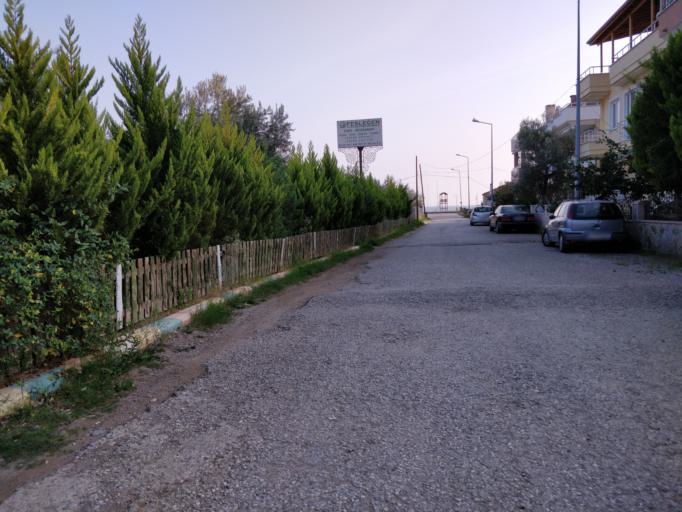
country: TR
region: Canakkale
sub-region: Merkez
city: Kucukkuyu
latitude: 39.5463
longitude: 26.6094
